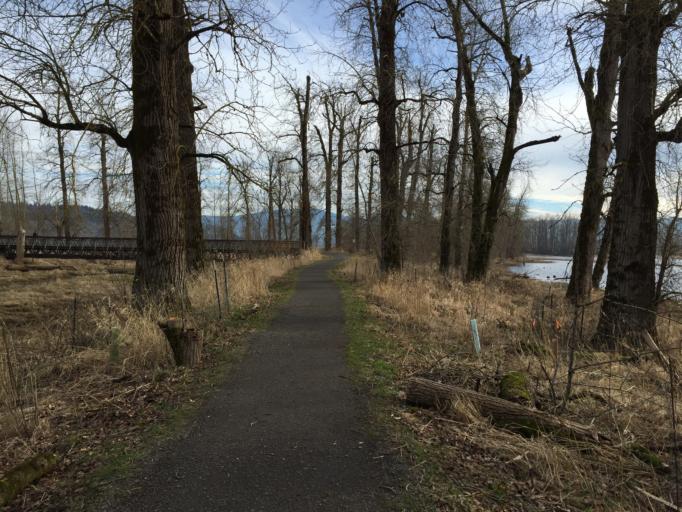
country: US
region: Washington
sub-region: Clark County
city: Washougal
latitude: 45.5630
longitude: -122.3127
